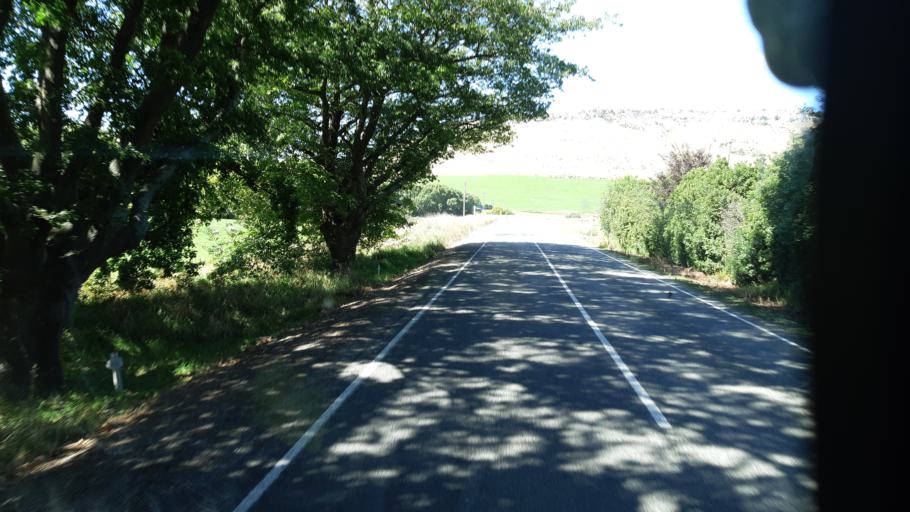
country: NZ
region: Otago
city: Oamaru
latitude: -45.0455
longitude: 170.8740
